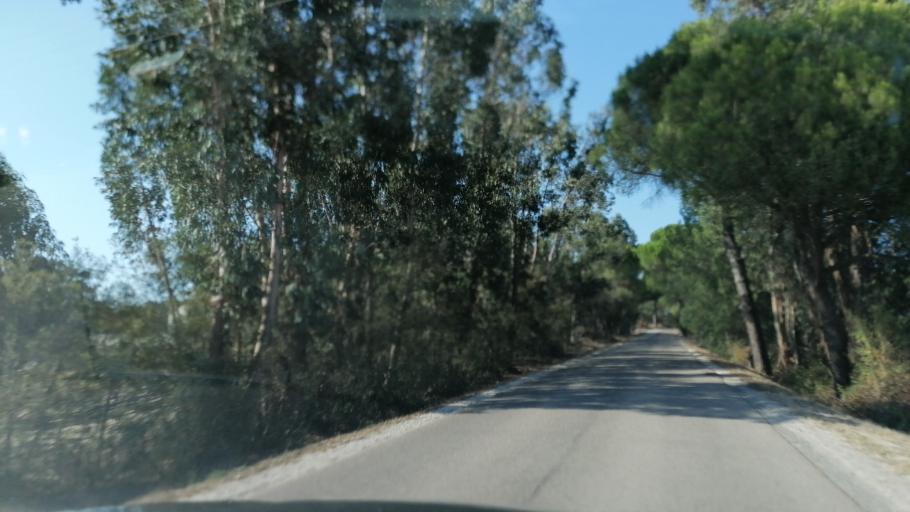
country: PT
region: Santarem
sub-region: Coruche
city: Coruche
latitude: 38.8044
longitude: -8.5790
